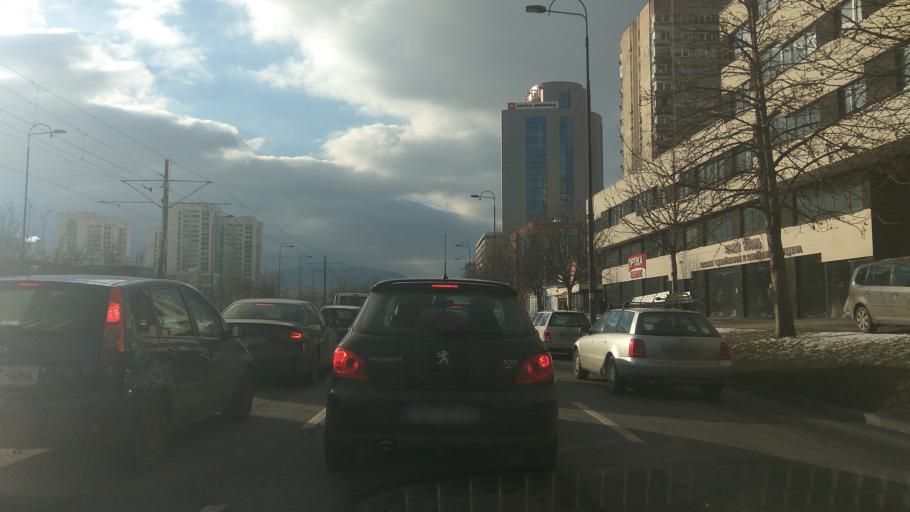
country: BA
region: Federation of Bosnia and Herzegovina
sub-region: Kanton Sarajevo
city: Sarajevo
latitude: 43.8498
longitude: 18.3699
